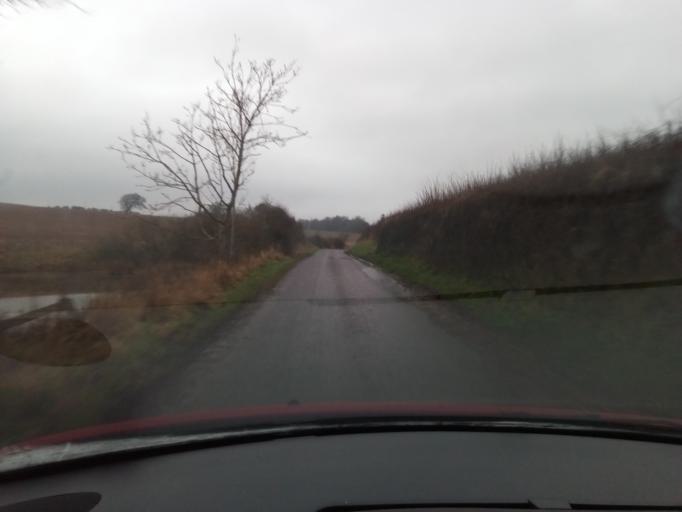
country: GB
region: Scotland
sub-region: The Scottish Borders
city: Kelso
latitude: 55.5464
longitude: -2.4346
